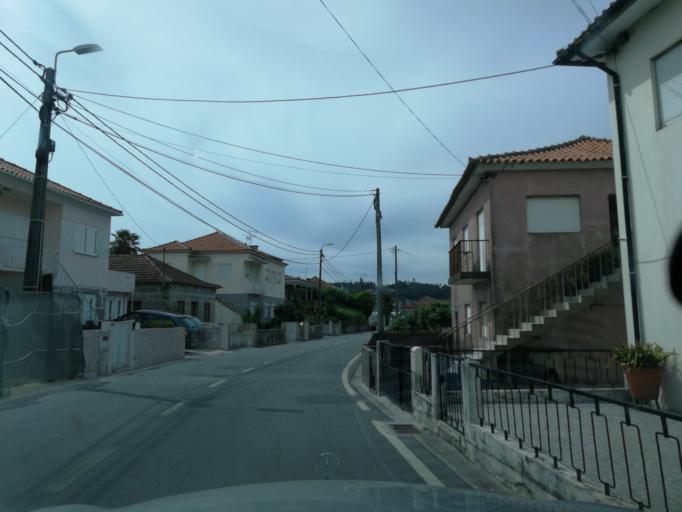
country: PT
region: Braga
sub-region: Vila Nova de Famalicao
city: Calendario
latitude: 41.4097
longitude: -8.5365
